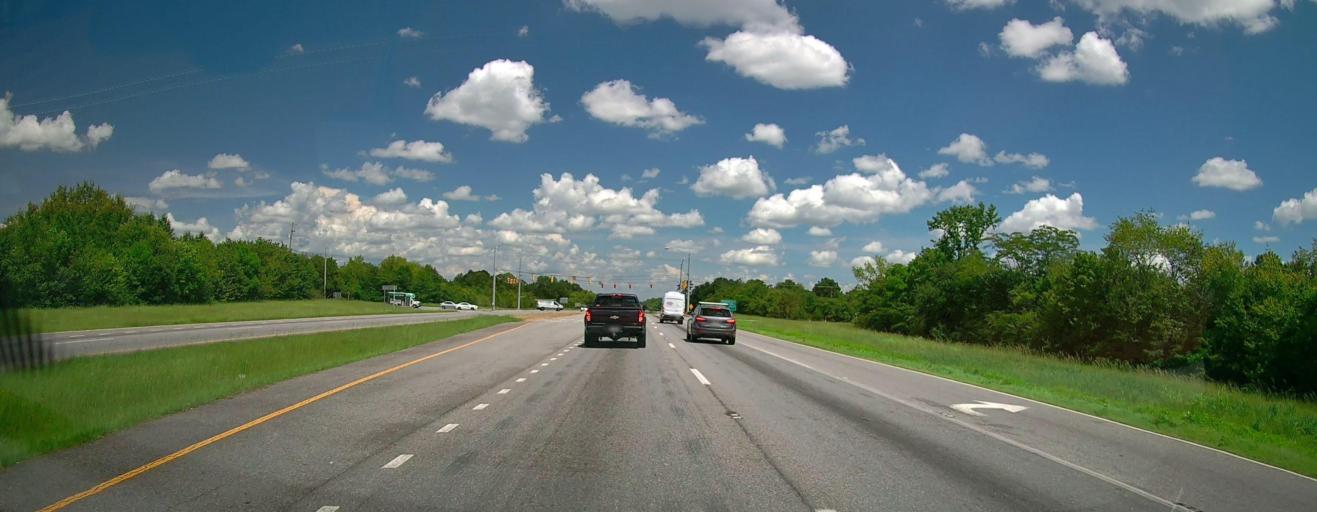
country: US
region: Alabama
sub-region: Montgomery County
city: Montgomery
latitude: 32.4227
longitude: -86.2703
